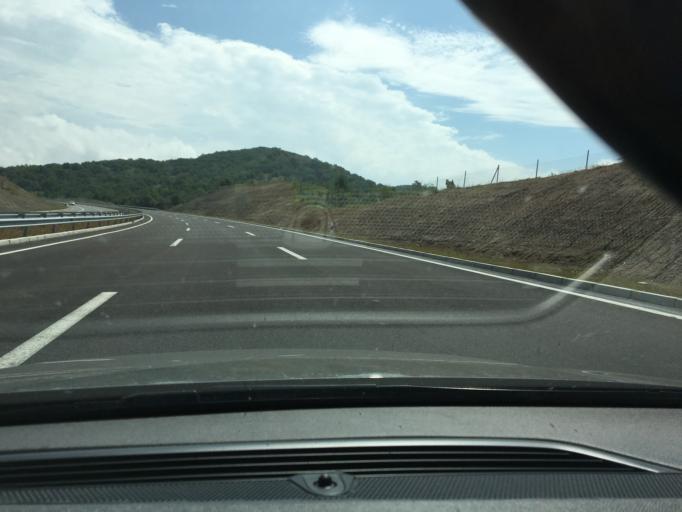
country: MK
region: Petrovec
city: Sredno Konjare
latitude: 41.9441
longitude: 21.7870
